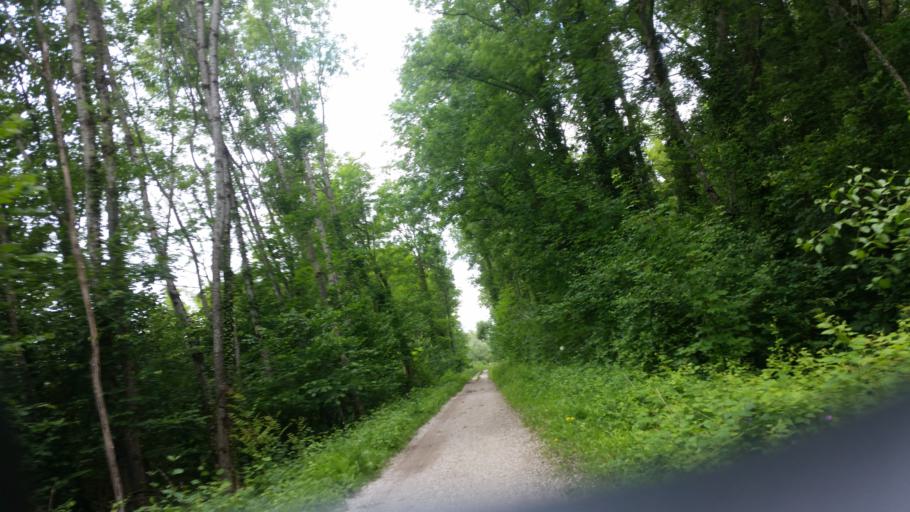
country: CH
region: Fribourg
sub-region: Broye District
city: Estavayer-le-Lac
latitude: 46.8331
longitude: 6.8105
